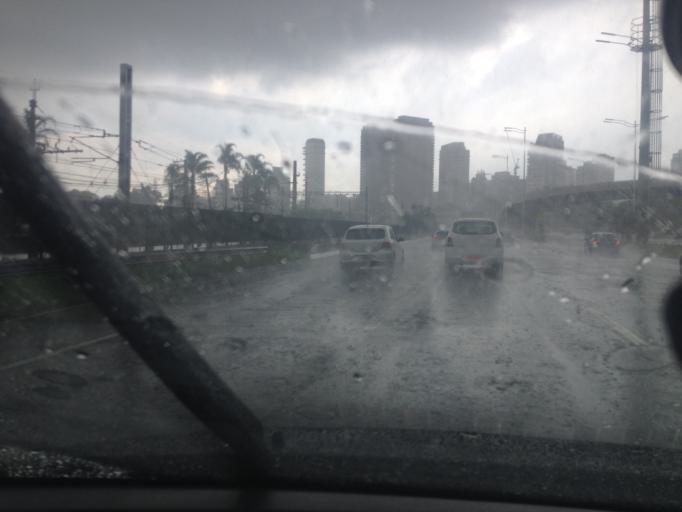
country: BR
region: Sao Paulo
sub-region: Sao Paulo
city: Sao Paulo
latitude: -23.5907
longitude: -46.6916
